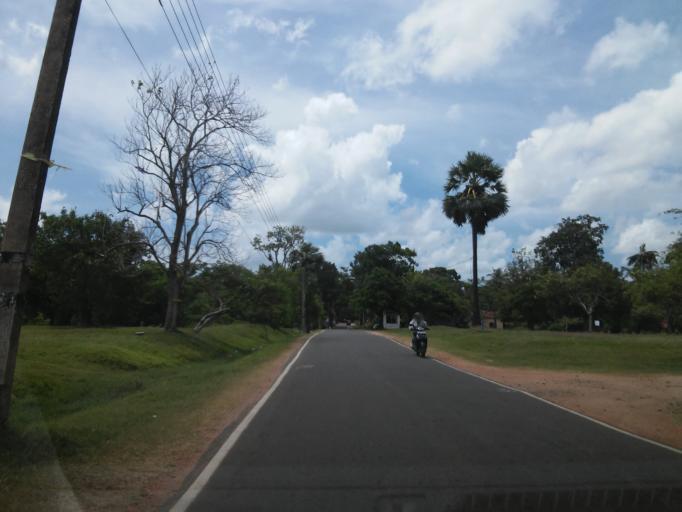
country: LK
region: North Central
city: Anuradhapura
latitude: 8.3545
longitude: 80.3987
